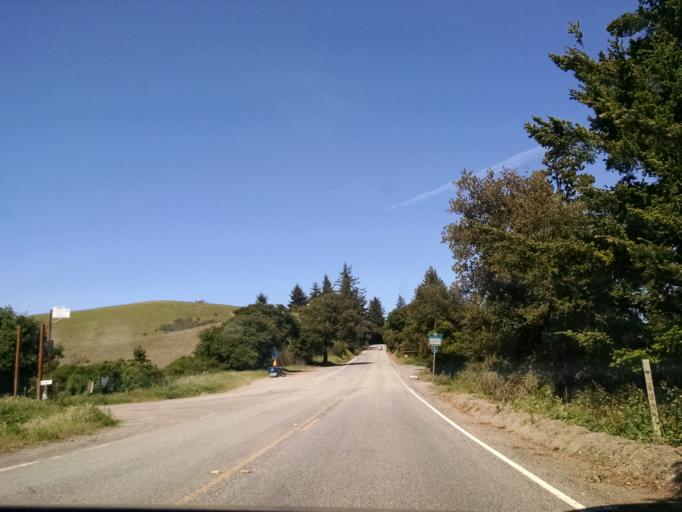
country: US
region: California
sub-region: San Mateo County
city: Portola Valley
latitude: 37.3411
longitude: -122.2200
